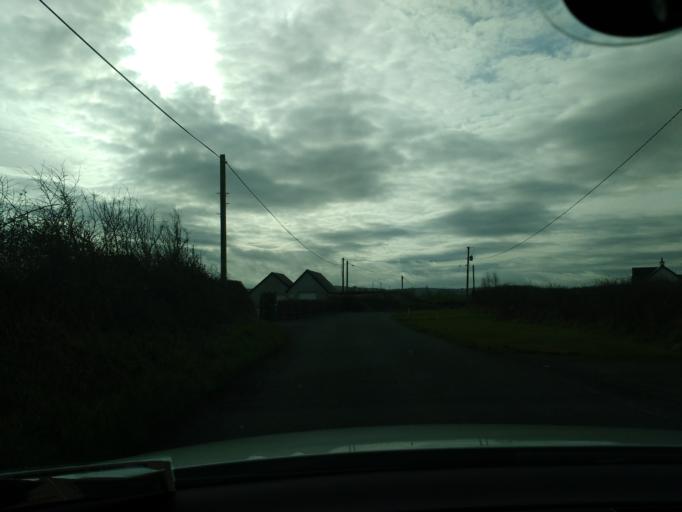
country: IE
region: Leinster
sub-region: Laois
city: Rathdowney
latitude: 52.6852
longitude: -7.6139
